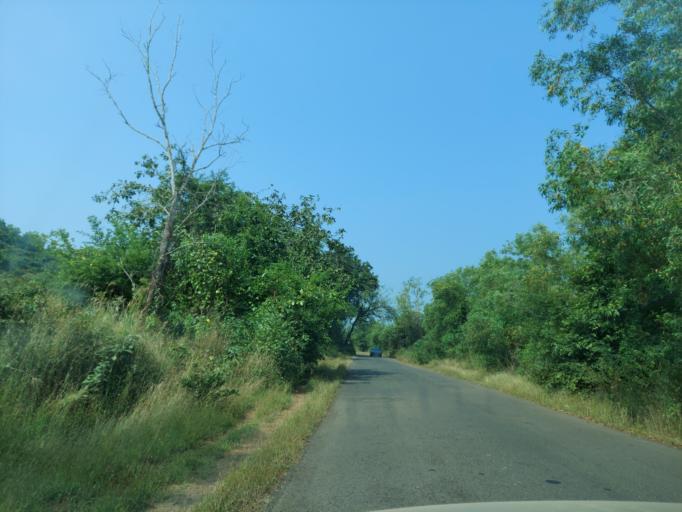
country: IN
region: Maharashtra
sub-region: Sindhudurg
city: Kudal
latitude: 15.9768
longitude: 73.6172
